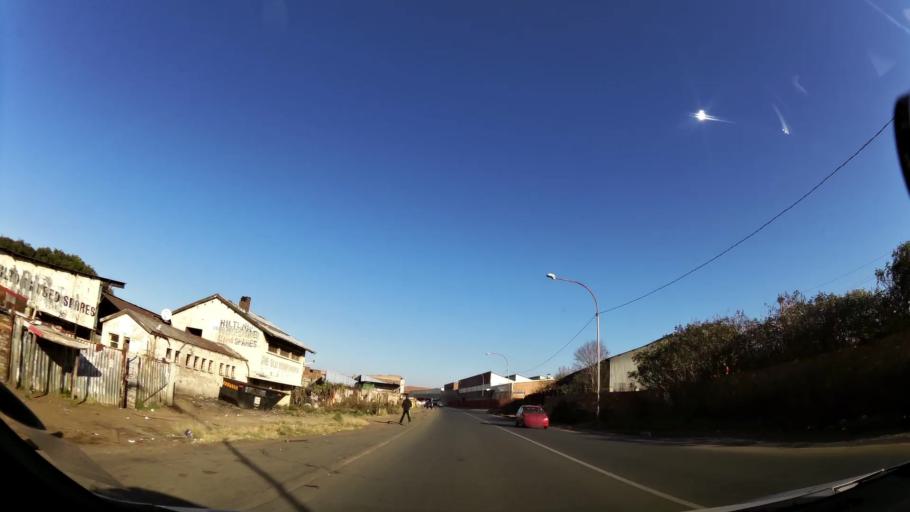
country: ZA
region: Gauteng
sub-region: City of Johannesburg Metropolitan Municipality
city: Johannesburg
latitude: -26.2040
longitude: 28.1066
